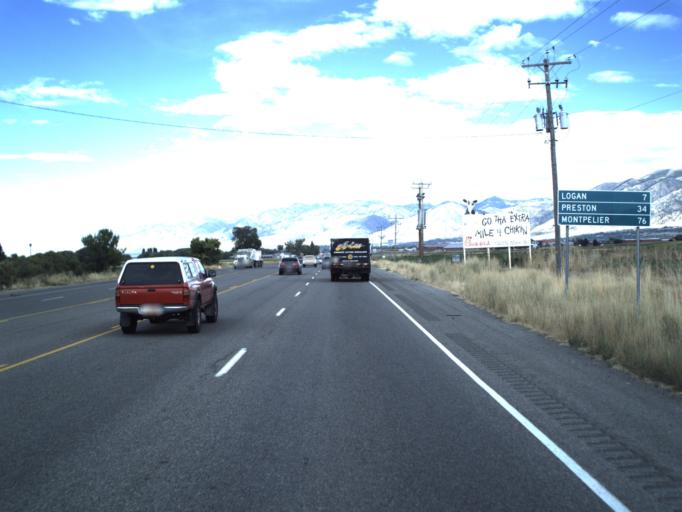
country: US
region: Utah
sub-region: Cache County
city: Wellsville
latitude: 41.6483
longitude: -111.9107
